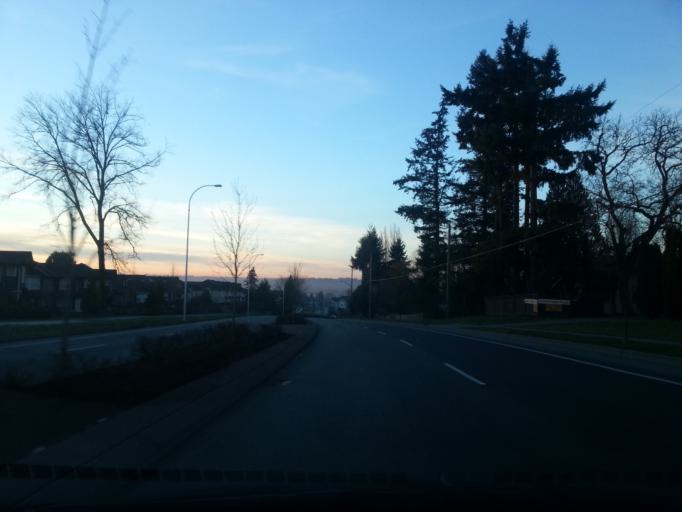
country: CA
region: British Columbia
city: Langley
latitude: 49.1315
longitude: -122.7198
